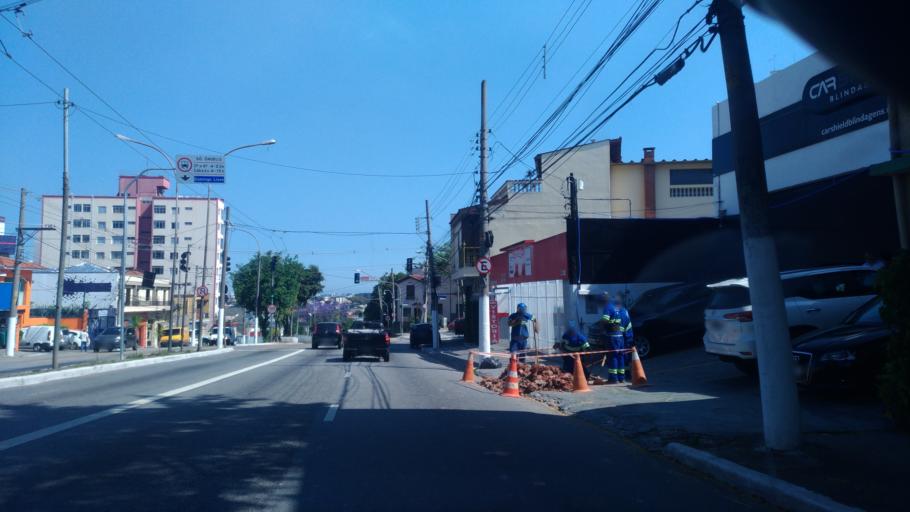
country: BR
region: Sao Paulo
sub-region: Sao Caetano Do Sul
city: Sao Caetano do Sul
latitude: -23.5785
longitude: -46.5871
